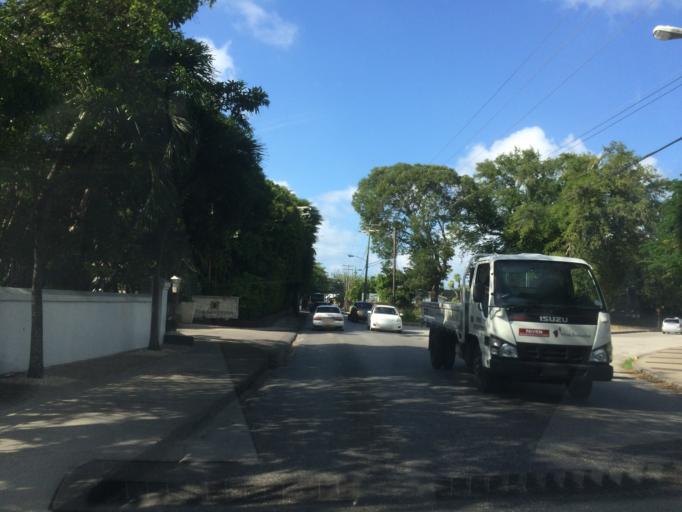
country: BB
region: Saint James
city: Holetown
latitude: 13.1889
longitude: -59.6369
